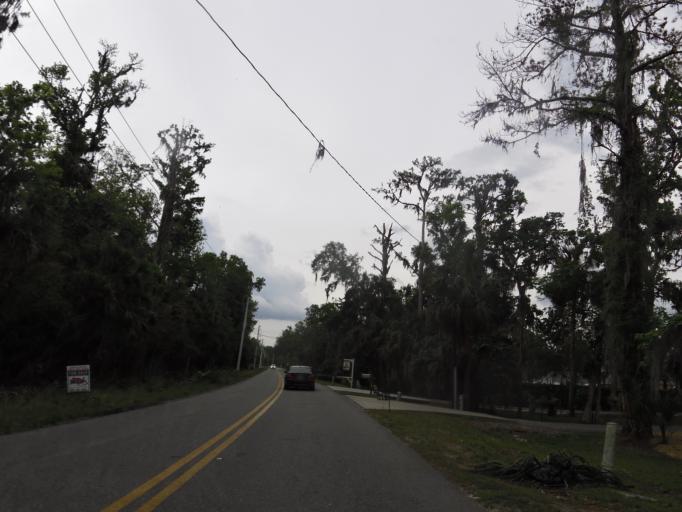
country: US
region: Florida
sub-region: Saint Johns County
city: Palm Valley
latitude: 30.1518
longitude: -81.3942
